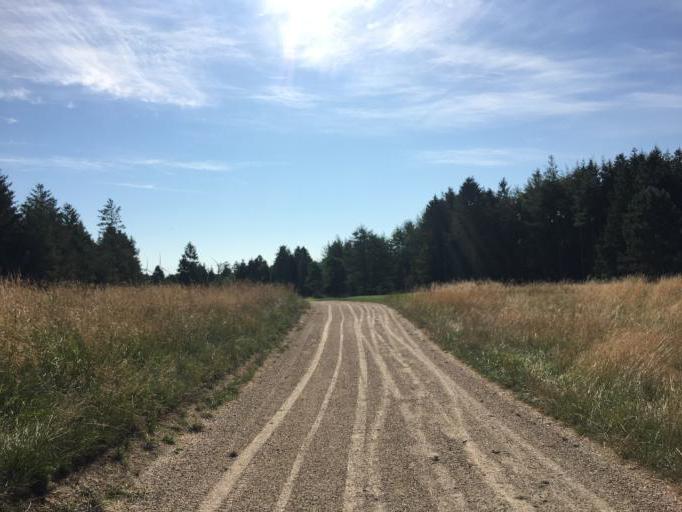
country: DK
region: Central Jutland
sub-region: Holstebro Kommune
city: Ulfborg
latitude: 56.3233
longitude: 8.4211
